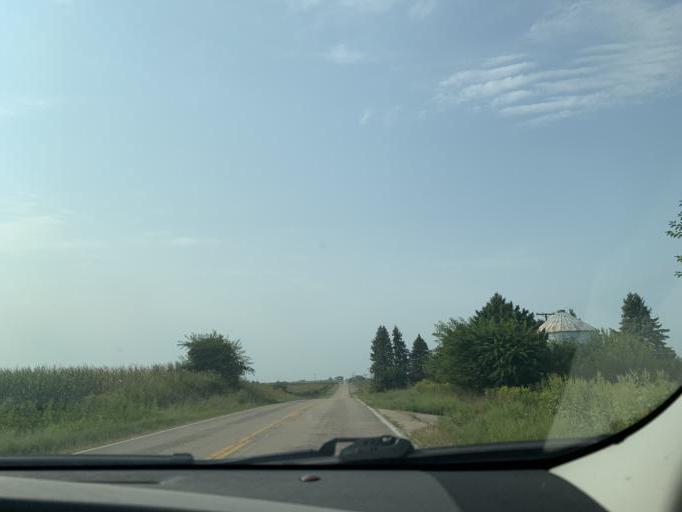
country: US
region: Illinois
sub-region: Whiteside County
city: Morrison
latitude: 41.8744
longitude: -89.9203
